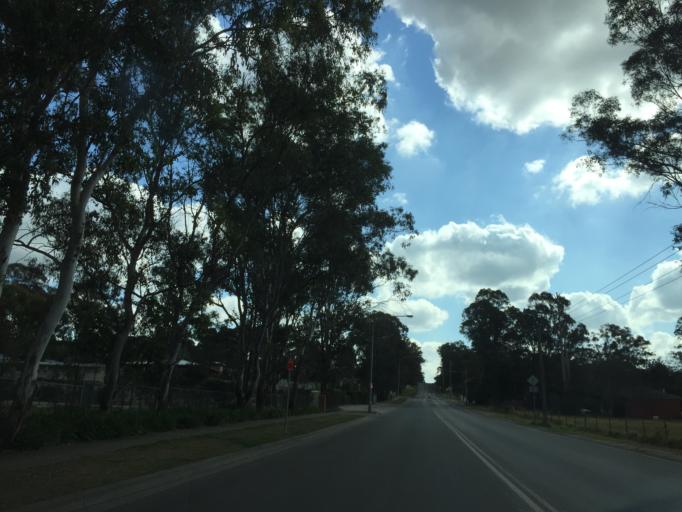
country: AU
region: New South Wales
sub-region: Blacktown
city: Rouse Hill
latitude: -33.6844
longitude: 150.9096
